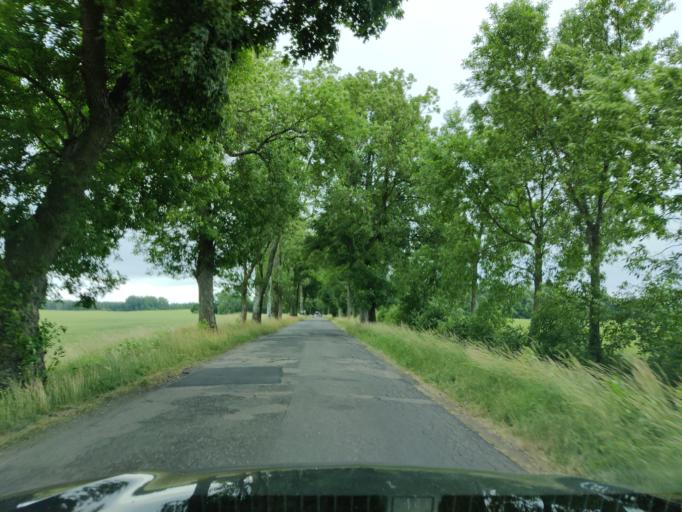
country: PL
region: Warmian-Masurian Voivodeship
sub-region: Powiat gizycki
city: Ryn
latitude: 53.9202
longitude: 21.5539
